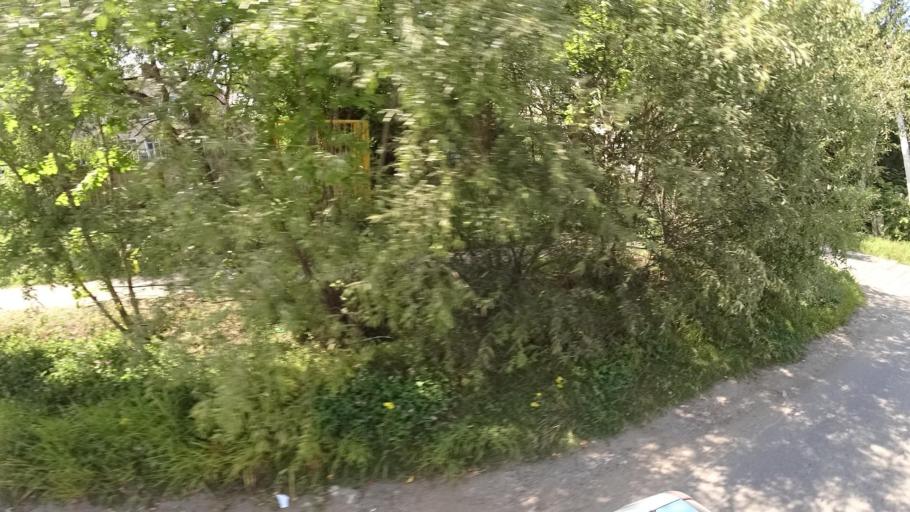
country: RU
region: Khabarovsk Krai
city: Khor
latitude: 47.9641
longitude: 135.0569
